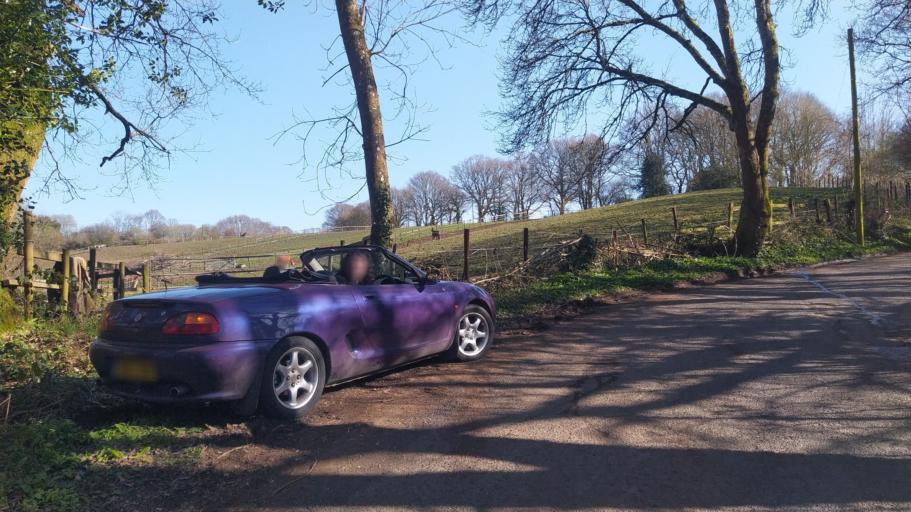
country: GB
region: England
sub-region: Dorset
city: Verwood
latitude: 50.8968
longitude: -1.8921
